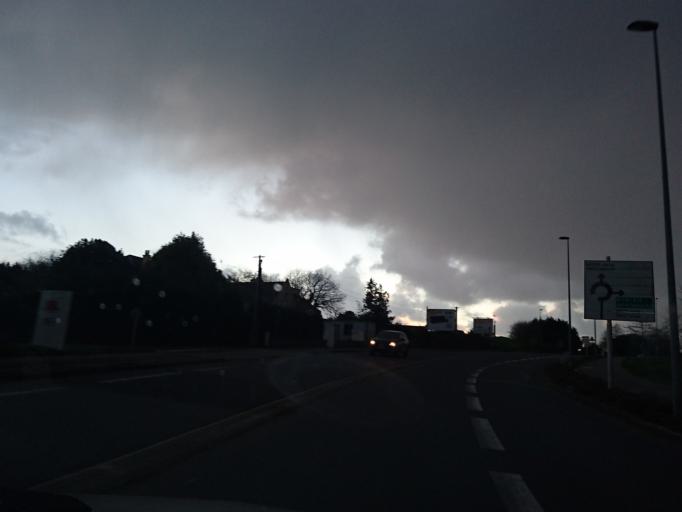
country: FR
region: Brittany
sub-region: Departement du Finistere
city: Le Relecq-Kerhuon
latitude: 48.4152
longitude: -4.4359
